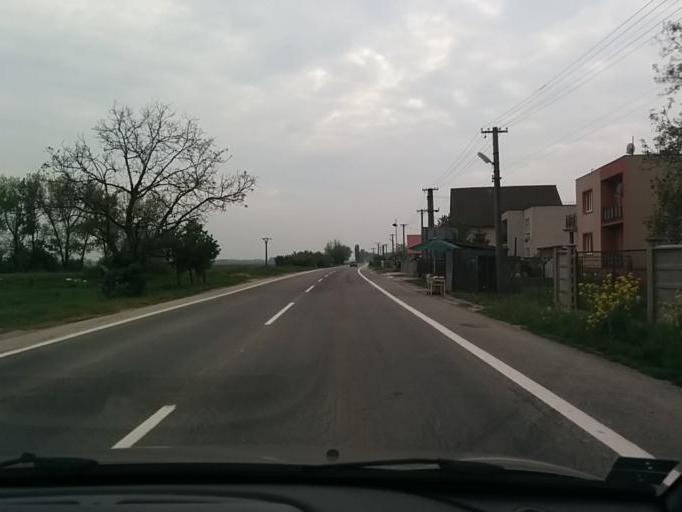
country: SK
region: Trnavsky
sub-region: Okres Galanta
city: Galanta
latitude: 48.2385
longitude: 17.6933
